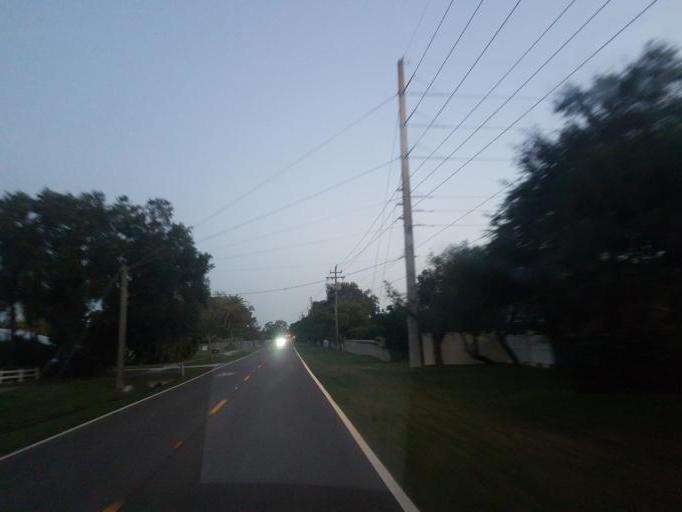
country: US
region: Florida
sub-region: Sarasota County
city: Lake Sarasota
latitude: 27.2780
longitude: -82.4563
